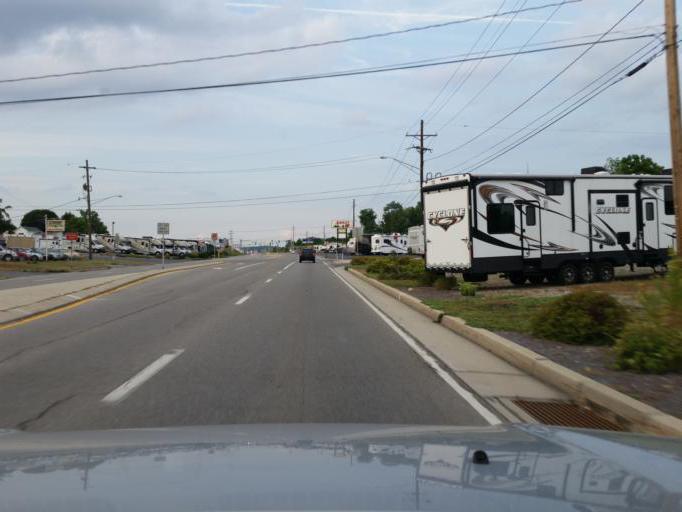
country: US
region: Pennsylvania
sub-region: Blair County
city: Duncansville
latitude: 40.4310
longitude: -78.4385
